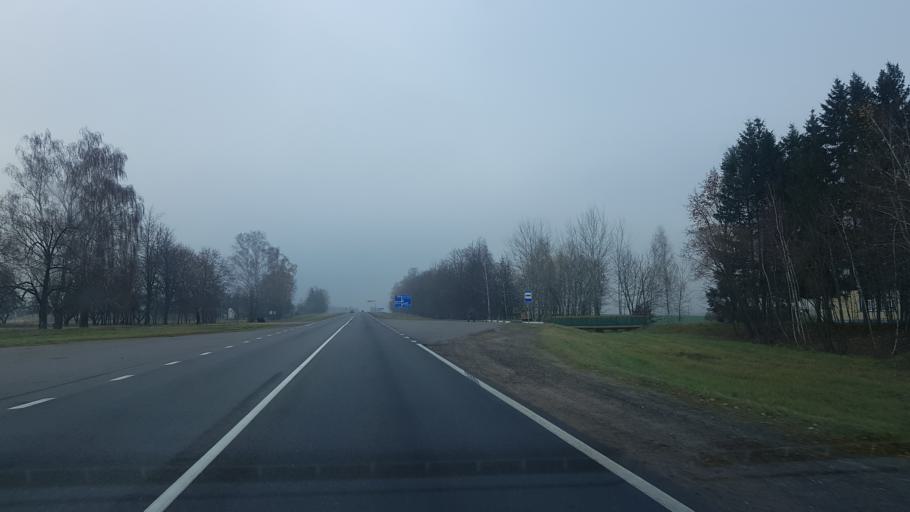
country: BY
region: Mogilev
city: Babruysk
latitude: 53.1778
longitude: 29.3463
